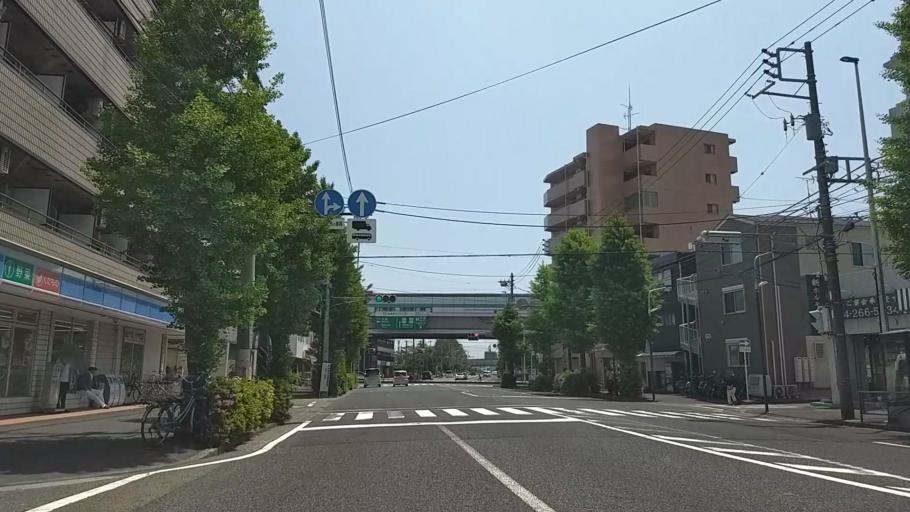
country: JP
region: Kanagawa
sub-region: Kawasaki-shi
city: Kawasaki
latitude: 35.5230
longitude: 139.7299
